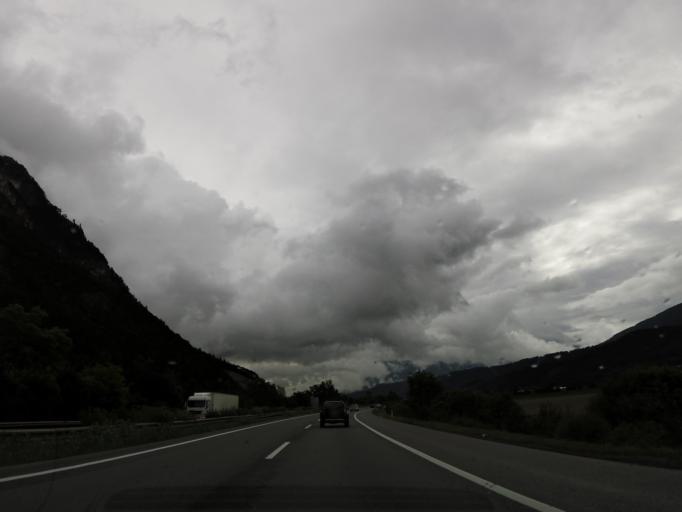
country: AT
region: Tyrol
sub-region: Politischer Bezirk Innsbruck Land
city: Kematen in Tirol
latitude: 47.2653
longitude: 11.2801
